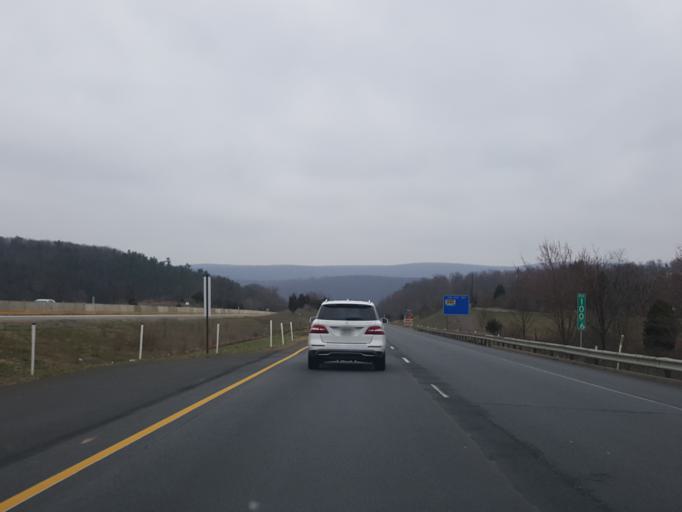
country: US
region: Pennsylvania
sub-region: Schuylkill County
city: Pine Grove
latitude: 40.5485
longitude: -76.4307
